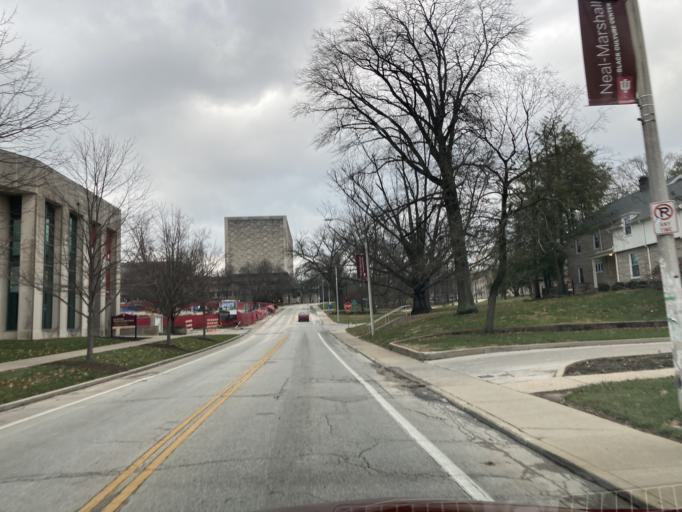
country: US
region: Indiana
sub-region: Monroe County
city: Bloomington
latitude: 39.1682
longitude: -86.5161
